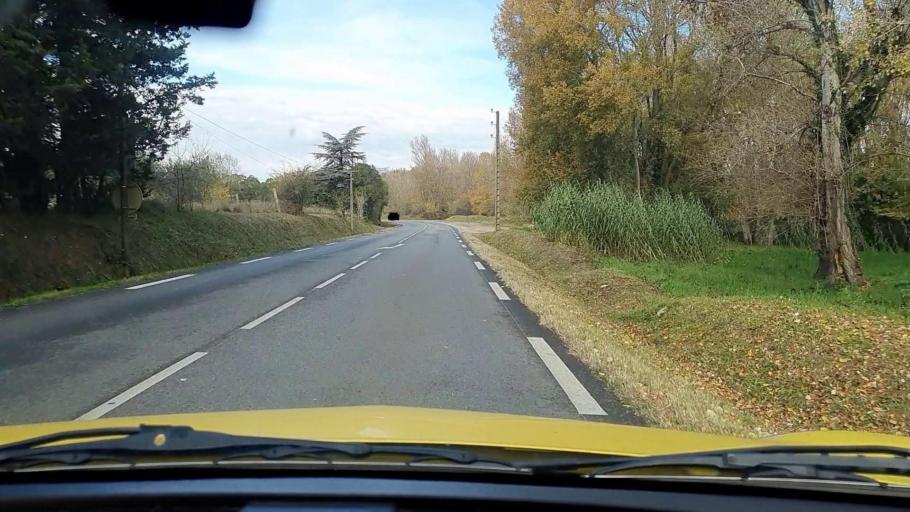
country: FR
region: Languedoc-Roussillon
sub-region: Departement du Gard
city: Comps
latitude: 43.8542
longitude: 4.5975
